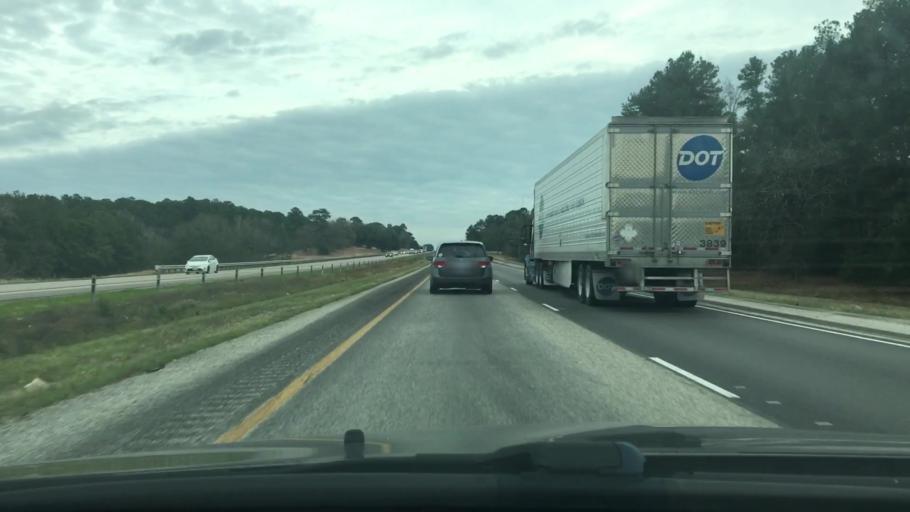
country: US
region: Texas
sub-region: Walker County
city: Huntsville
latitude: 30.8235
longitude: -95.7055
